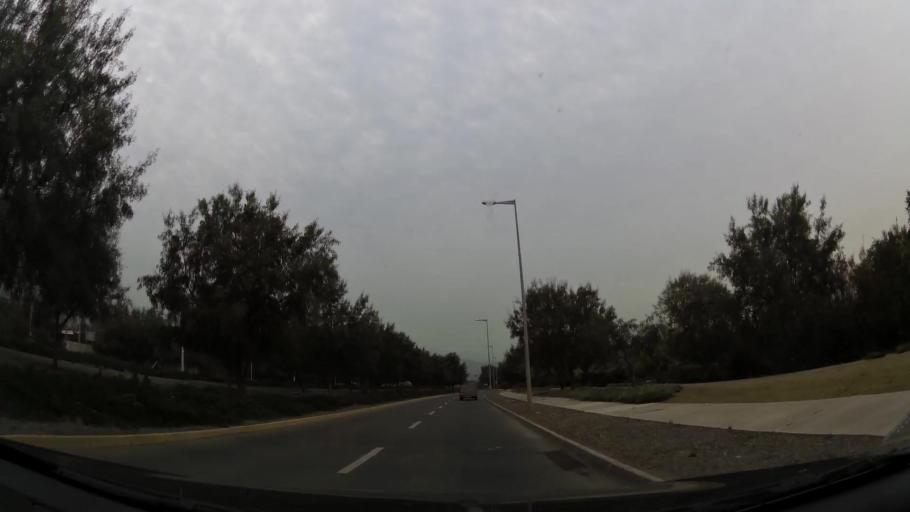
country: CL
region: Santiago Metropolitan
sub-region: Provincia de Chacabuco
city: Chicureo Abajo
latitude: -33.2609
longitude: -70.6266
